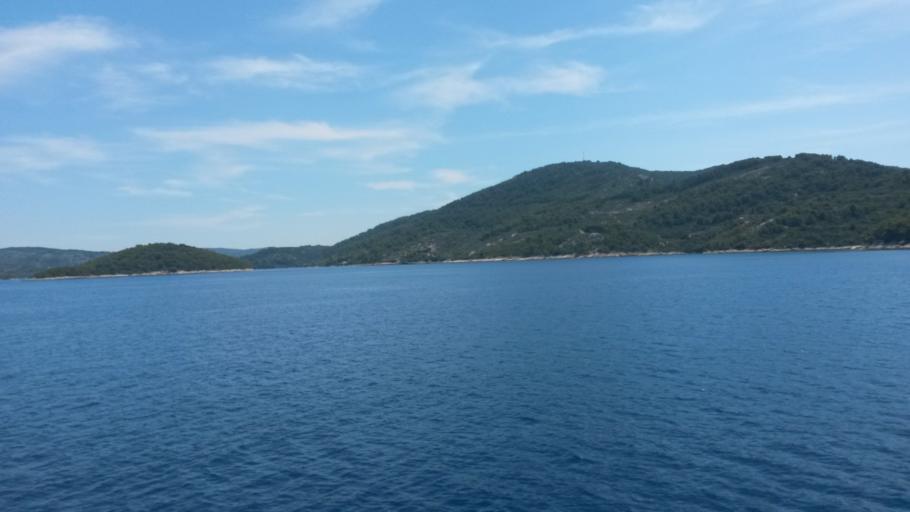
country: HR
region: Dubrovacko-Neretvanska
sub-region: Grad Dubrovnik
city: Vela Luka
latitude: 42.9587
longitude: 16.6589
